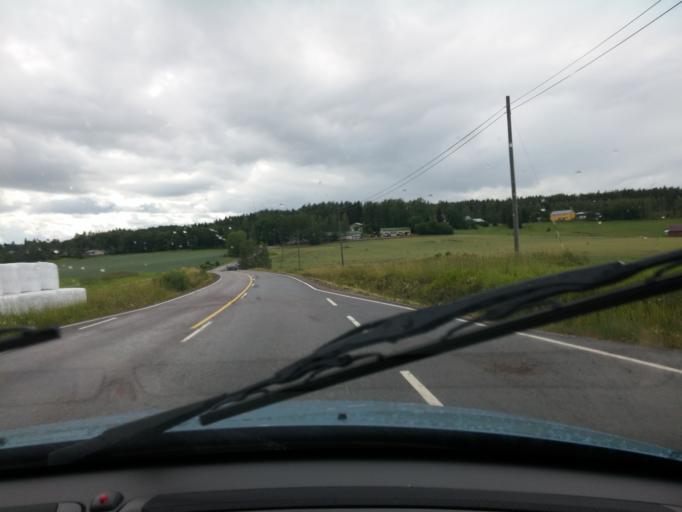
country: FI
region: Uusimaa
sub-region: Porvoo
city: Askola
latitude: 60.5548
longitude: 25.7040
